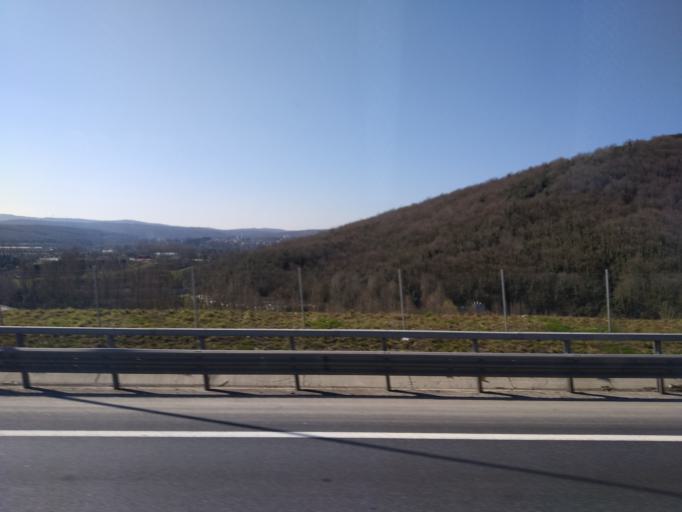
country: TR
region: Istanbul
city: Mahmut Sevket Pasa
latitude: 41.1361
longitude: 29.2866
